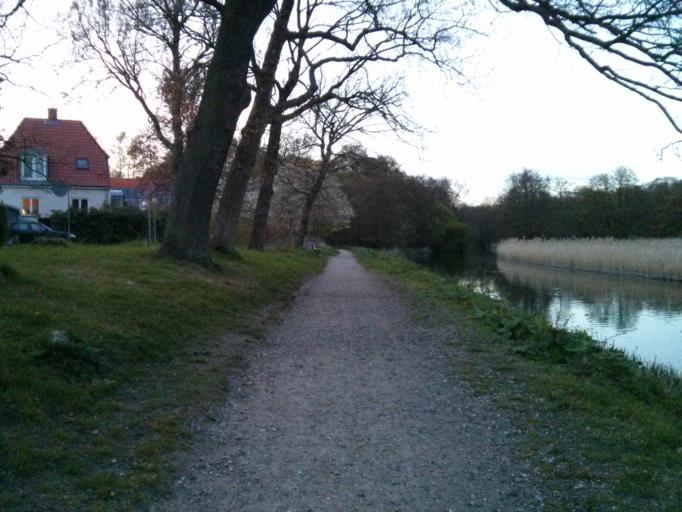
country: DK
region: Zealand
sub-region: Naestved Kommune
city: Naestved
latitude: 55.2349
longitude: 11.7504
